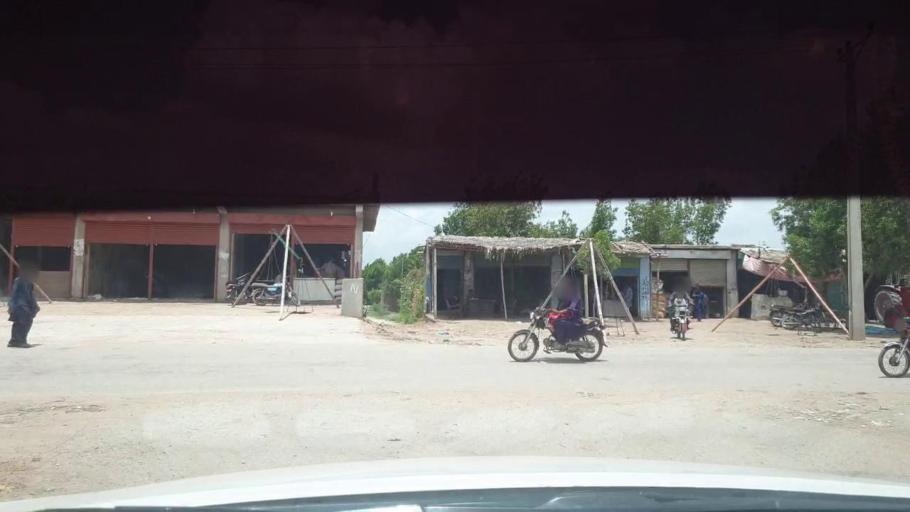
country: PK
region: Sindh
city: Kadhan
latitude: 24.4740
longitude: 68.9897
